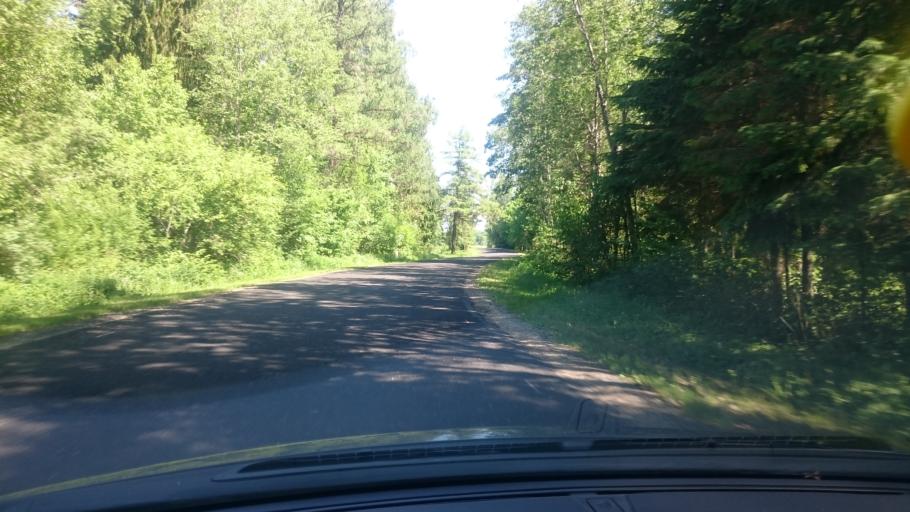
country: EE
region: Harju
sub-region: Rae vald
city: Vaida
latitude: 59.2178
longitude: 24.9574
